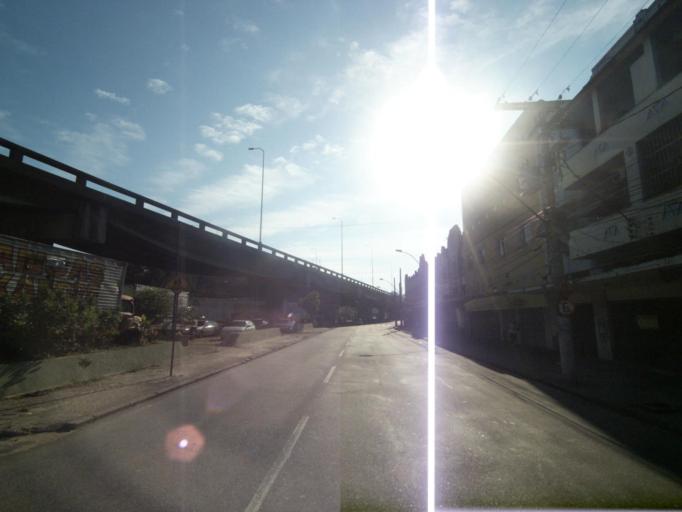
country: BR
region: Rio de Janeiro
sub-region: Niteroi
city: Niteroi
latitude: -22.8813
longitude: -43.1106
